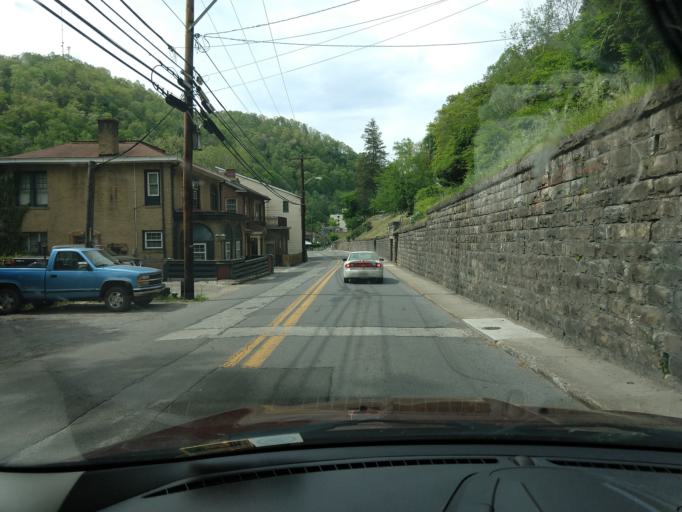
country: US
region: West Virginia
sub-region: McDowell County
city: Welch
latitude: 37.4273
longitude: -81.5844
